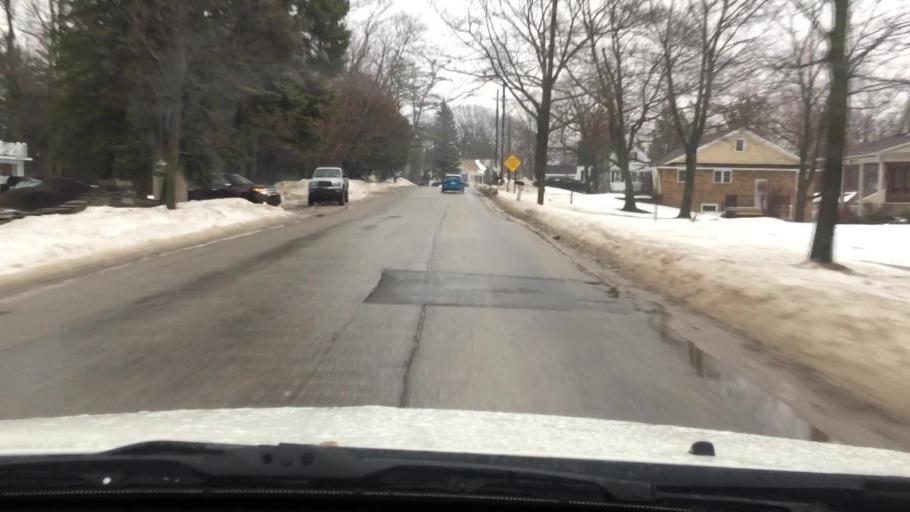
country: US
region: Michigan
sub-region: Charlevoix County
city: Charlevoix
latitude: 45.3149
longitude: -85.2721
